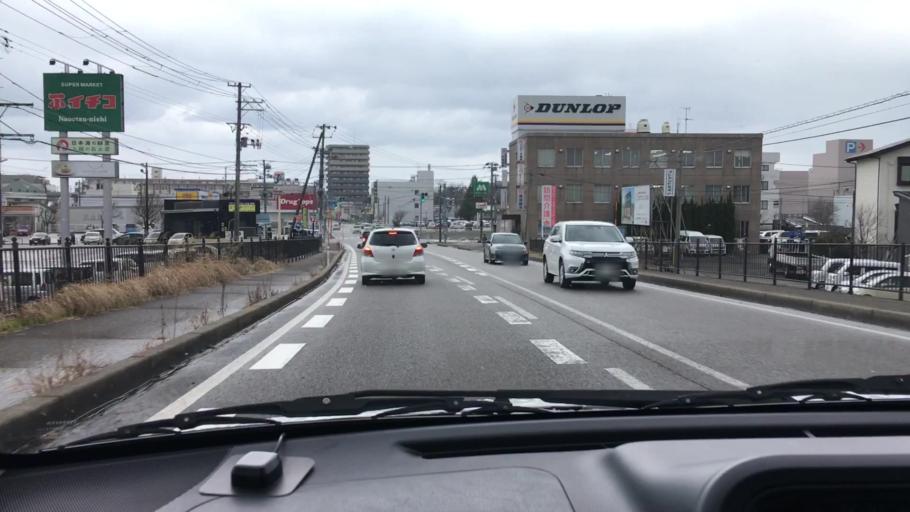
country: JP
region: Niigata
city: Joetsu
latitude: 37.1684
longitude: 138.2369
